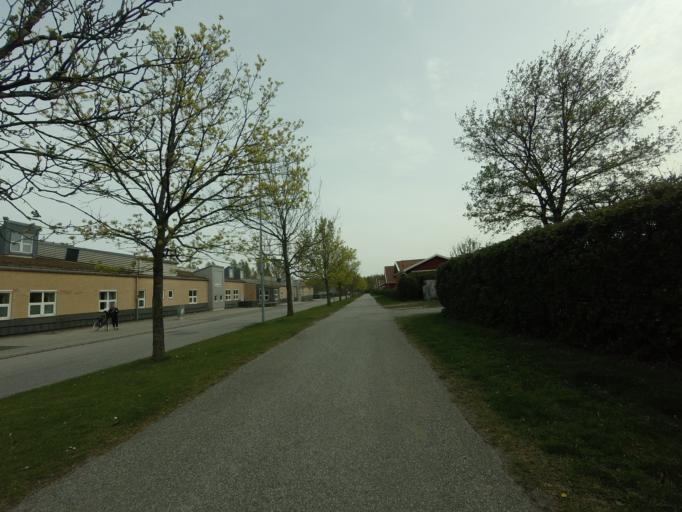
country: SE
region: Skane
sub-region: Lunds Kommun
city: Lund
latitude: 55.7245
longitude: 13.1669
